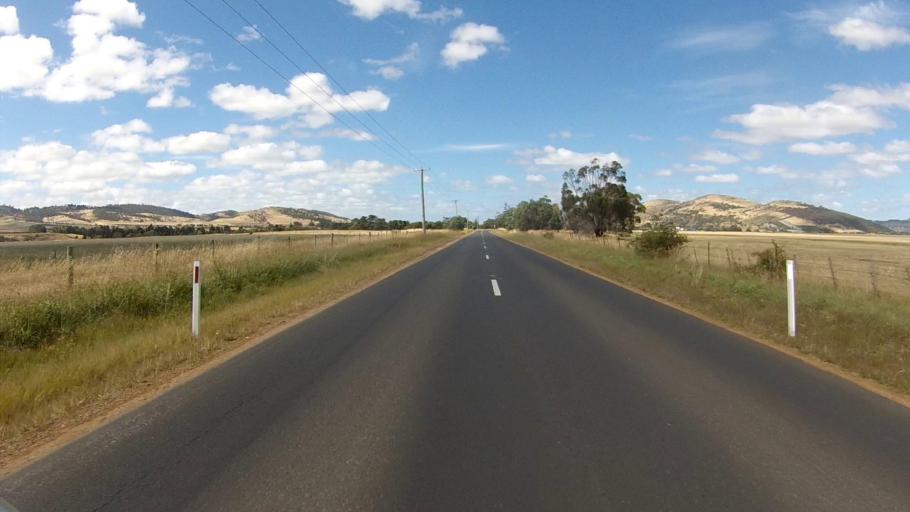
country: AU
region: Tasmania
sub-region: Clarence
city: Cambridge
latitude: -42.7212
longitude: 147.4342
